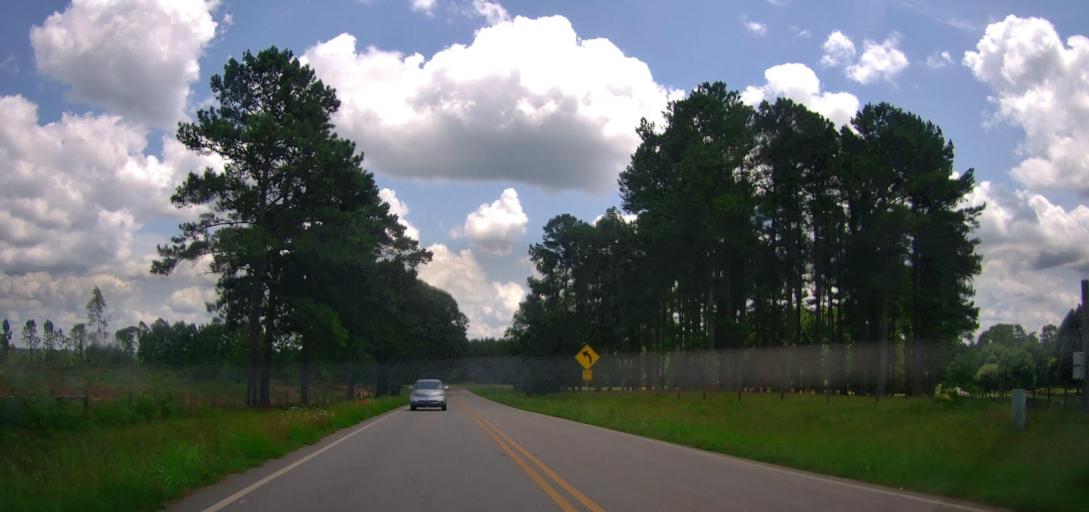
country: US
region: Georgia
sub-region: Troup County
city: Hogansville
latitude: 33.1518
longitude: -84.8535
